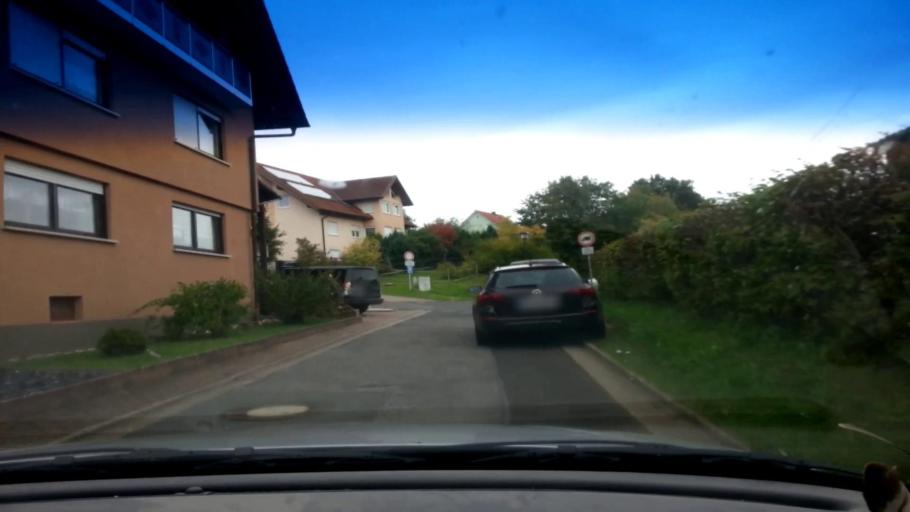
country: DE
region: Bavaria
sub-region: Upper Franconia
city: Gerach
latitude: 50.0302
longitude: 10.8049
